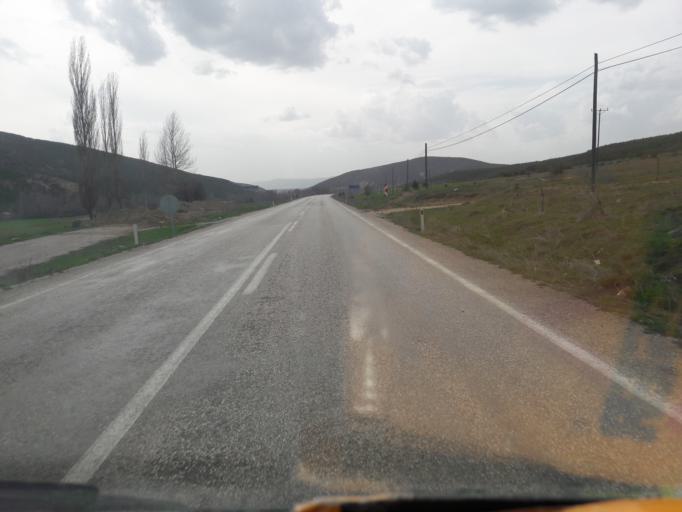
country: TR
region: Gumushane
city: Siran
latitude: 40.1727
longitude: 39.1686
